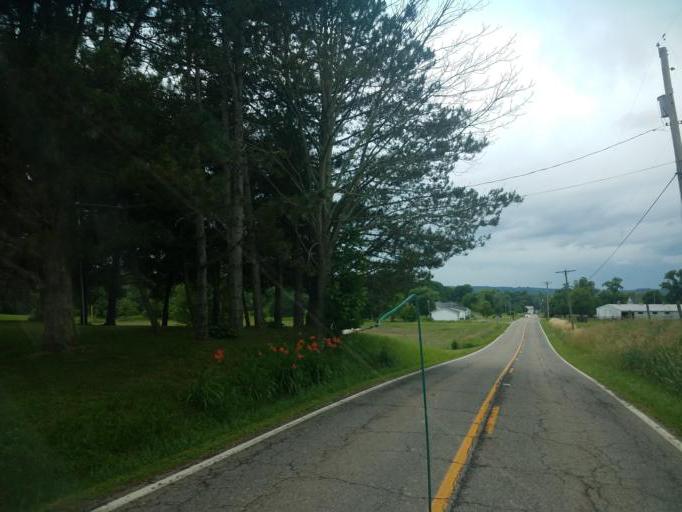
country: US
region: Ohio
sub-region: Columbiana County
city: Leetonia
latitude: 40.8532
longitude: -80.7754
